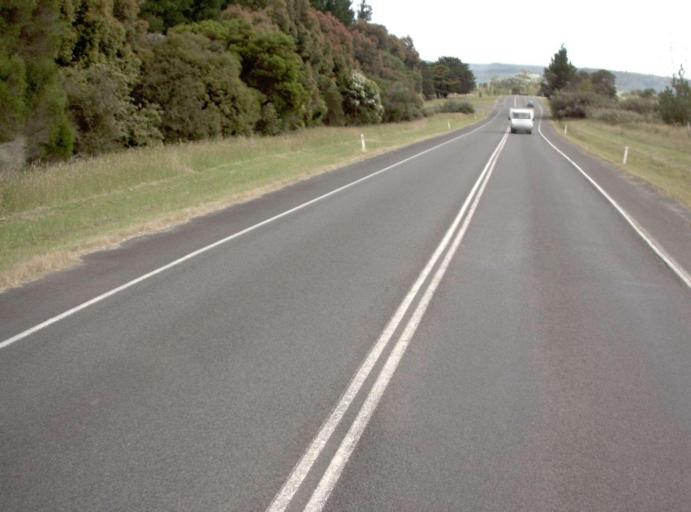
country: AU
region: Victoria
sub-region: Latrobe
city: Morwell
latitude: -38.1937
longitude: 146.4502
